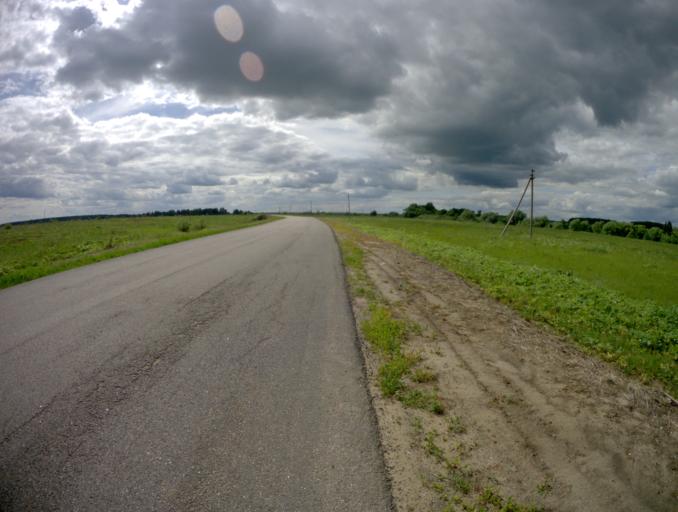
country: RU
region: Vladimir
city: Stavrovo
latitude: 56.2764
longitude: 39.8194
